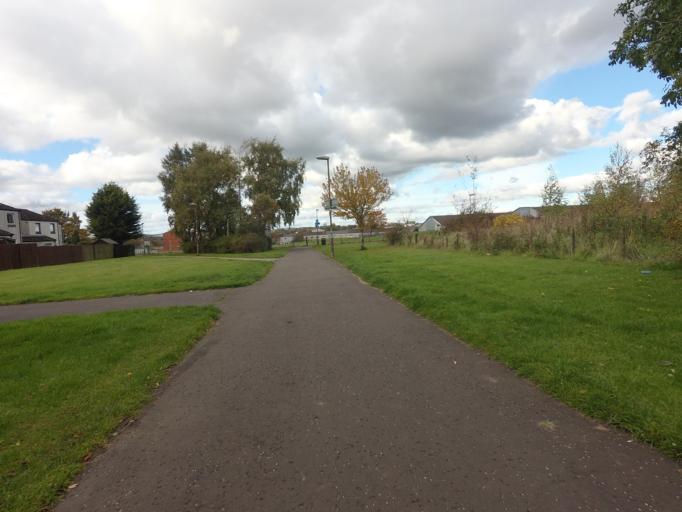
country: GB
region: Scotland
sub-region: West Lothian
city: Mid Calder
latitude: 55.8810
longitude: -3.4997
